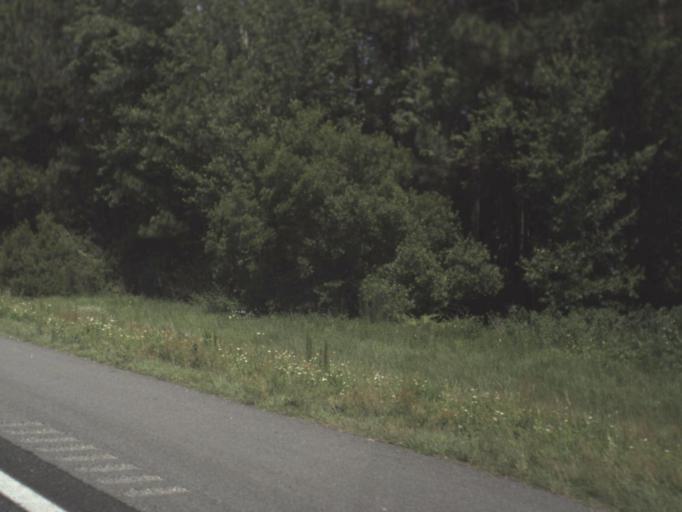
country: US
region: Florida
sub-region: Duval County
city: Baldwin
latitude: 30.3019
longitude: -81.9233
